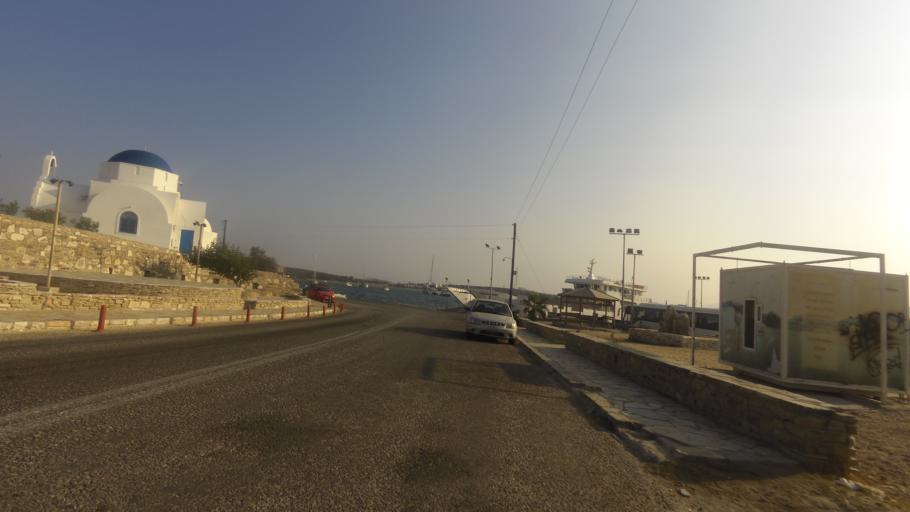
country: GR
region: South Aegean
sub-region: Nomos Kykladon
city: Antiparos
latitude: 37.0389
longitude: 25.0852
